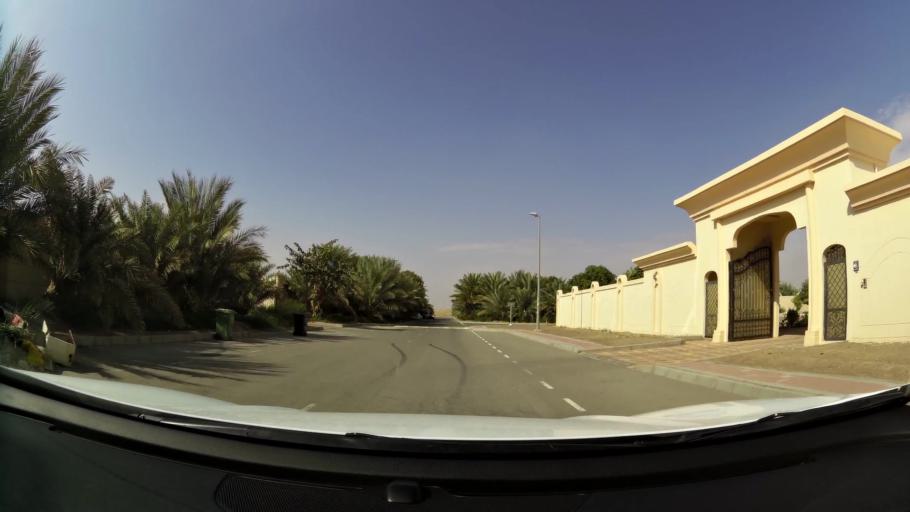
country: AE
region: Abu Dhabi
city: Al Ain
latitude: 24.0964
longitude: 55.9248
